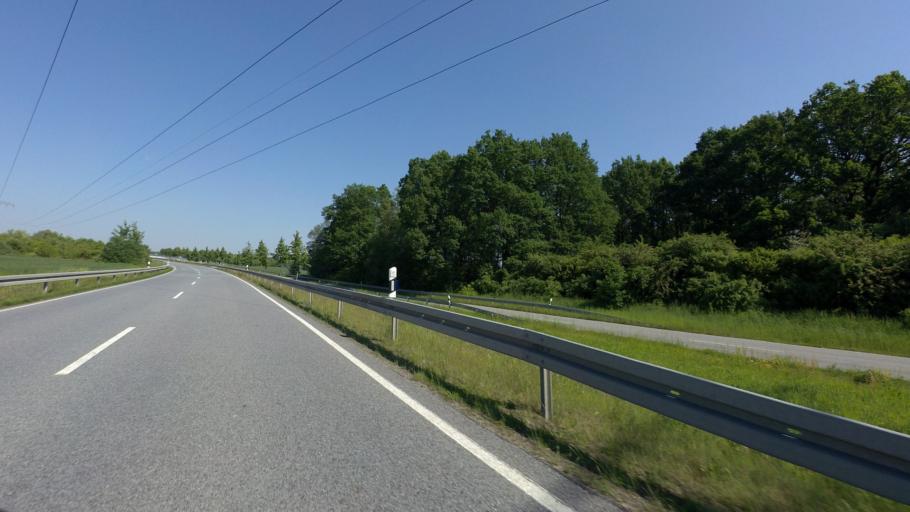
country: DE
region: Saxony
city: Nebelschutz
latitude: 51.2507
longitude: 14.1664
